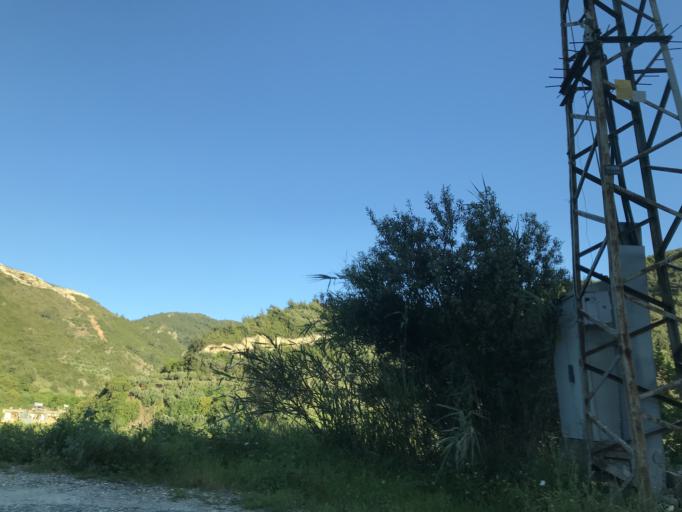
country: TR
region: Hatay
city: Buyukcat
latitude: 36.0766
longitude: 36.0440
